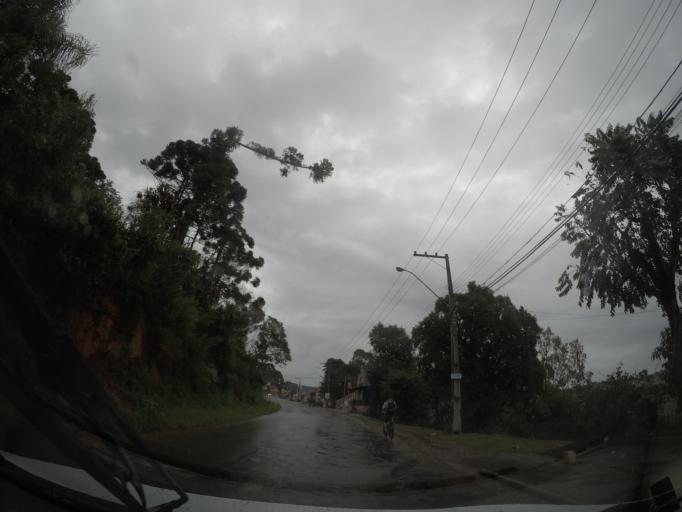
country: BR
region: Parana
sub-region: Curitiba
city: Curitiba
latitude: -25.4592
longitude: -49.3892
